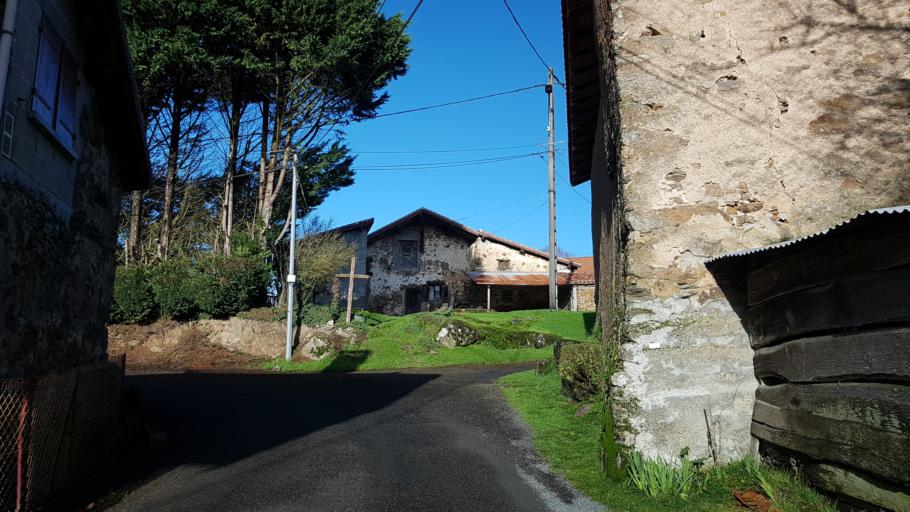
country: FR
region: Poitou-Charentes
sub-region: Departement de la Charente
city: Etagnac
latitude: 45.8976
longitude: 0.8031
